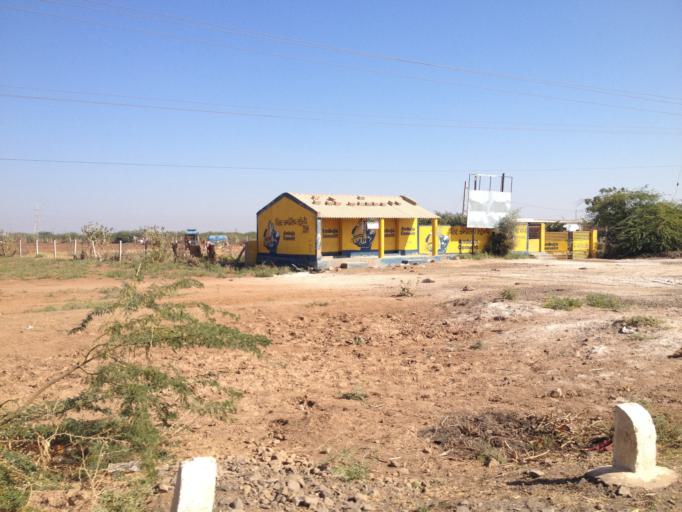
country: IN
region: Gujarat
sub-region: Kachchh
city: Anjar
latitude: 23.1846
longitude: 69.9123
